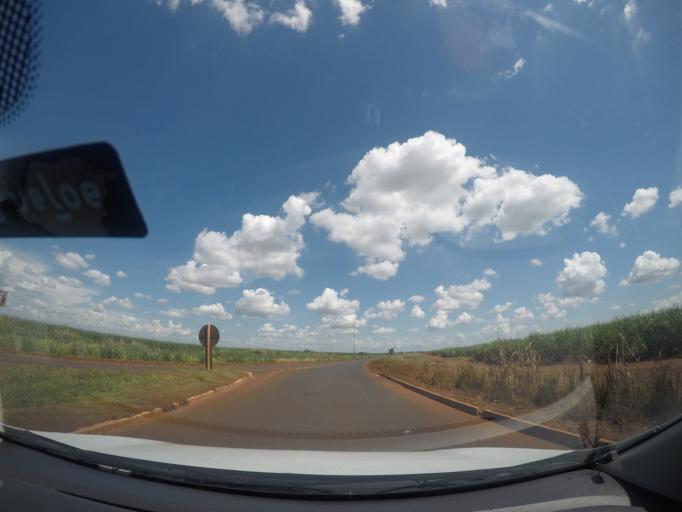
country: BR
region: Minas Gerais
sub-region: Frutal
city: Frutal
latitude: -19.8199
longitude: -48.7319
